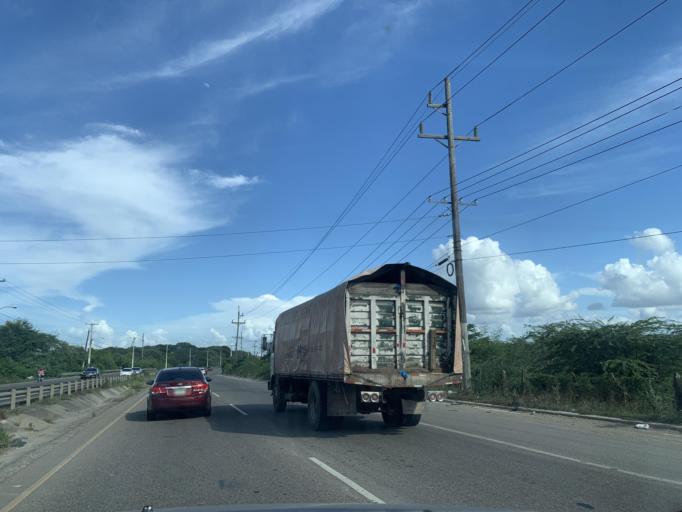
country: DO
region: Santiago
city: Villa Gonzalez
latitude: 19.5260
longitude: -70.7716
